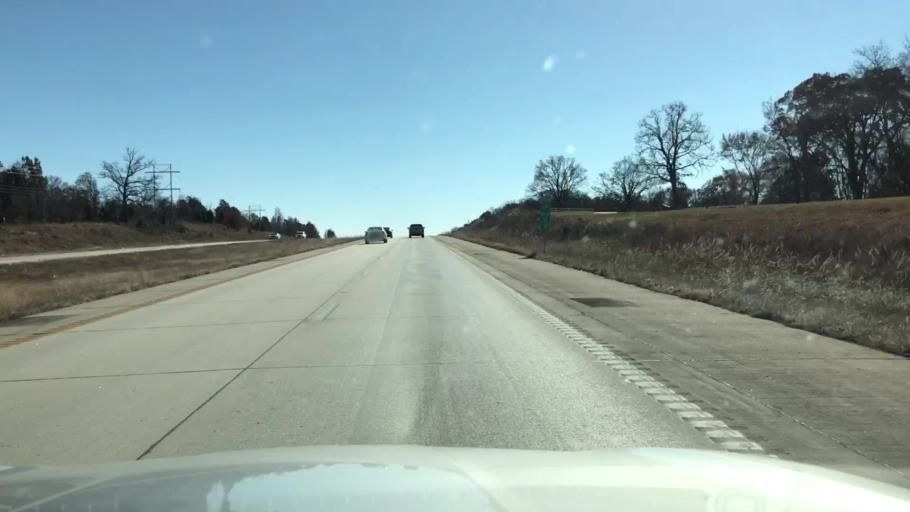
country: US
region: Missouri
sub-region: Jasper County
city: Duquesne
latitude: 37.0265
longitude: -94.4301
